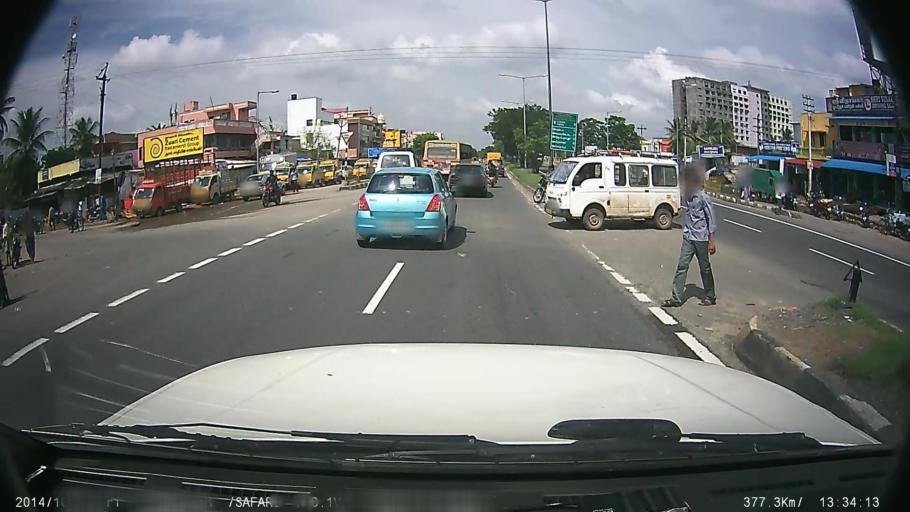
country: IN
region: Tamil Nadu
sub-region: Kancheepuram
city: Singapperumalkovil
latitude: 12.7626
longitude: 80.0041
